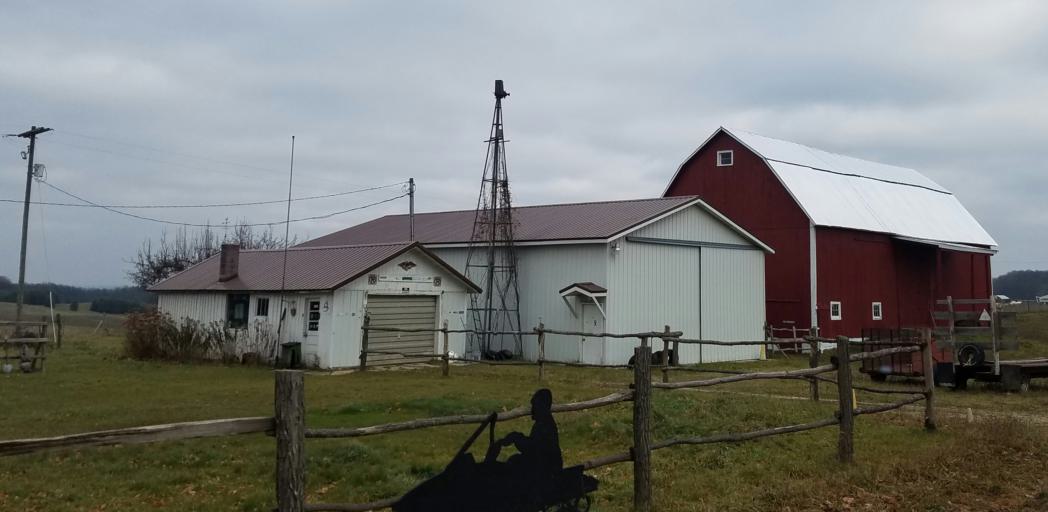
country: US
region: Michigan
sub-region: Wexford County
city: Manton
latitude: 44.3963
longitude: -85.4869
